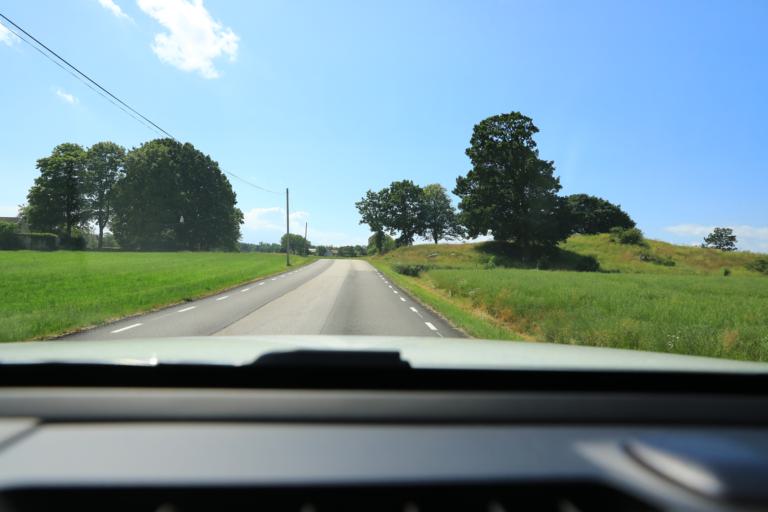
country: SE
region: Halland
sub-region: Varbergs Kommun
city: Tvaaker
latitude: 57.1028
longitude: 12.4105
